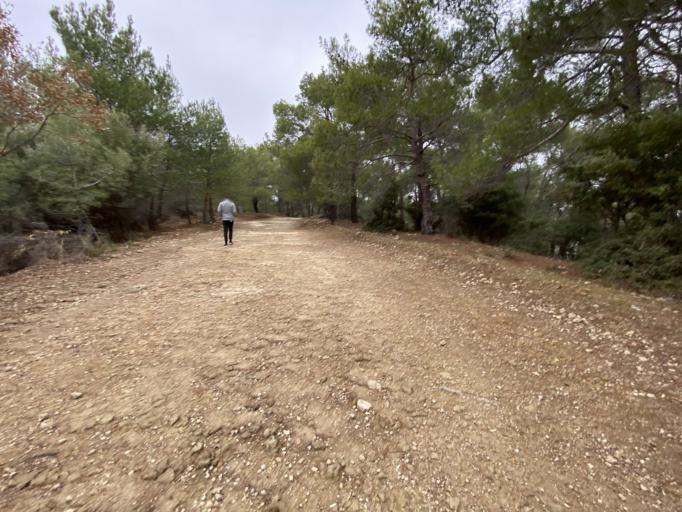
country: TR
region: Canakkale
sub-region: Merkez
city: Kucukkuyu
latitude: 39.5625
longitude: 26.6171
